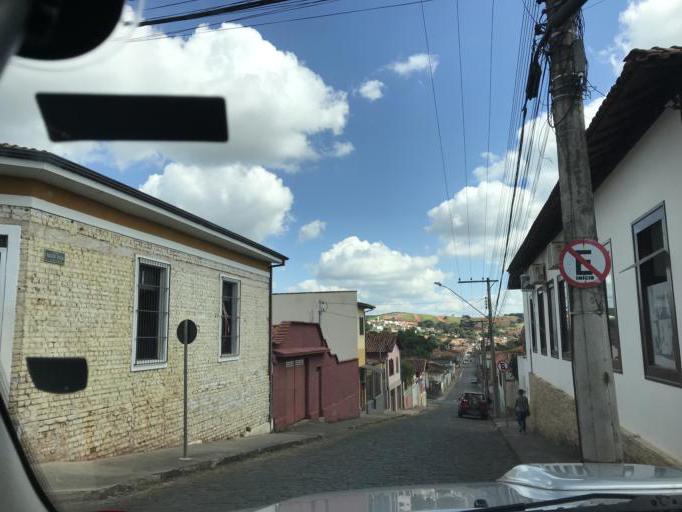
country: BR
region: Minas Gerais
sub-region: Campanha
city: Campanha
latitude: -21.8334
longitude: -45.4017
